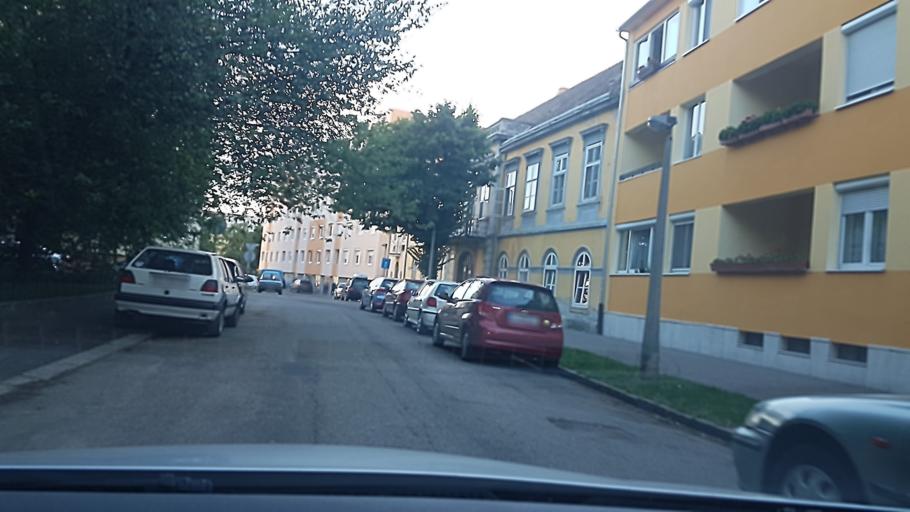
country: HU
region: Gyor-Moson-Sopron
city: Sopron
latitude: 47.6794
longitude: 16.5942
